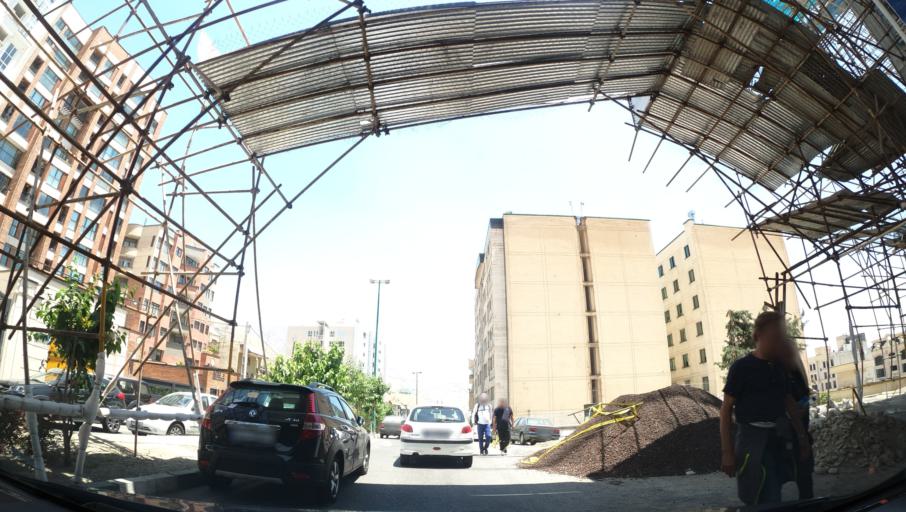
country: IR
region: Tehran
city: Tajrish
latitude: 35.8122
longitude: 51.3961
